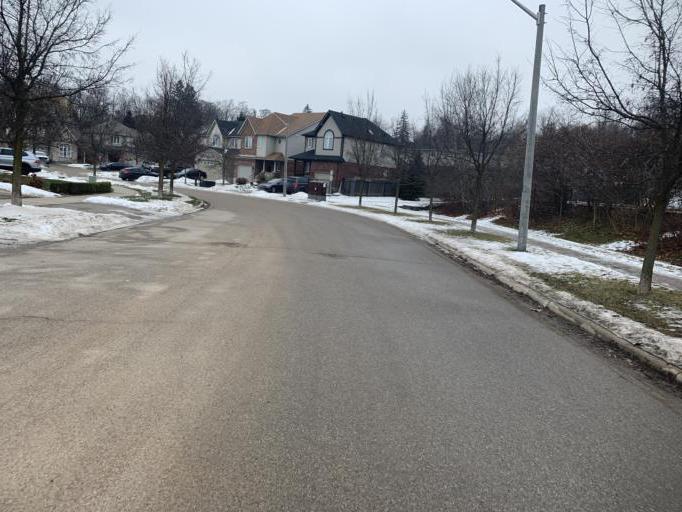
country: CA
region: Ontario
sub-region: Halton
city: Milton
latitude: 43.6598
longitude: -79.9203
